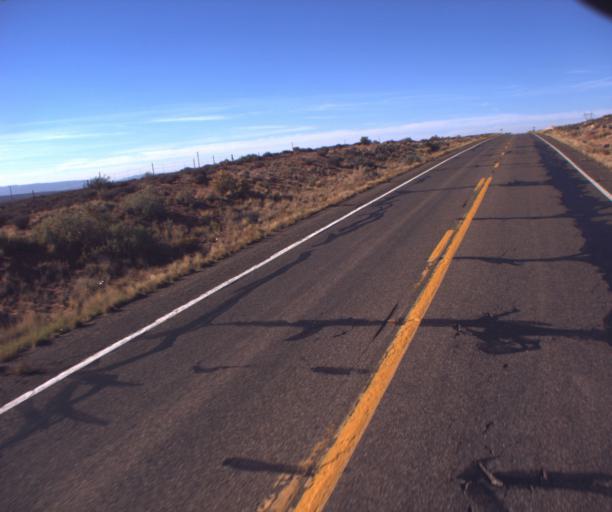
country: US
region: Arizona
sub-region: Coconino County
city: LeChee
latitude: 36.7930
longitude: -111.2978
